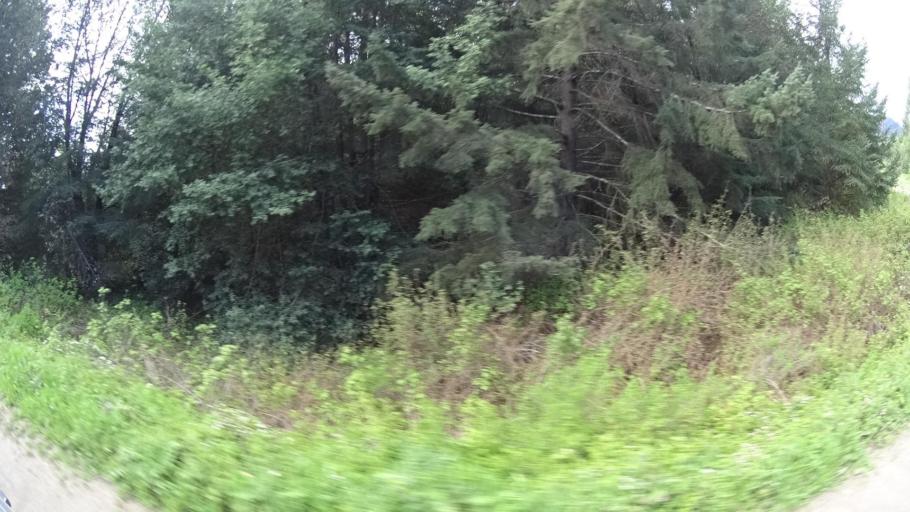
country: US
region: California
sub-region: Humboldt County
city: Redway
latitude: 40.2106
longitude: -123.6727
